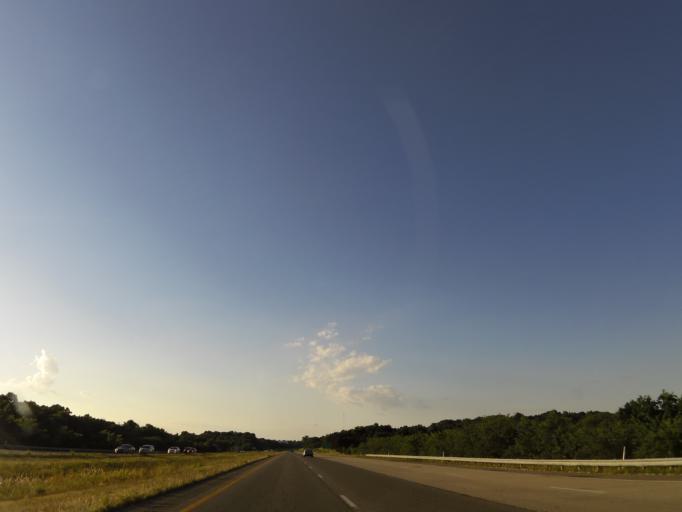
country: US
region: Tennessee
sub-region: Wilson County
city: Rural Hill
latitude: 36.0475
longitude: -86.4302
